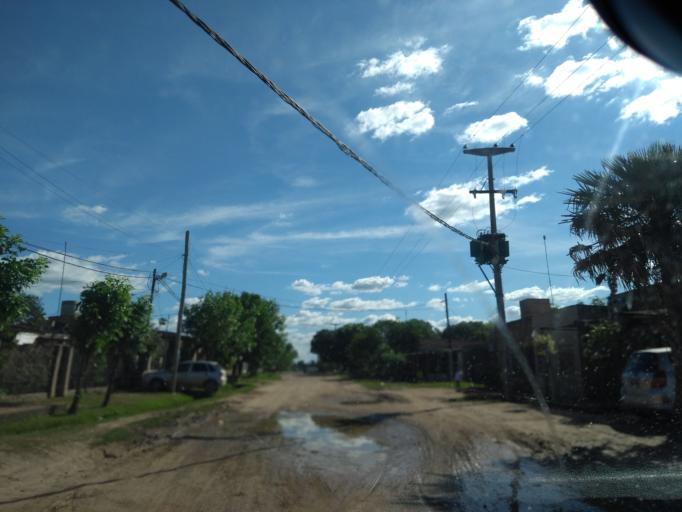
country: AR
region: Chaco
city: Resistencia
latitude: -27.4563
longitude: -58.9637
